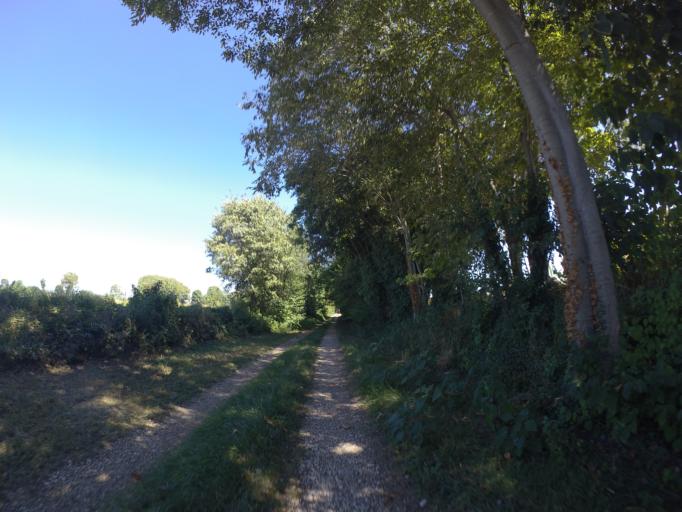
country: IT
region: Friuli Venezia Giulia
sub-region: Provincia di Udine
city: Bertiolo
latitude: 45.9544
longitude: 13.0873
